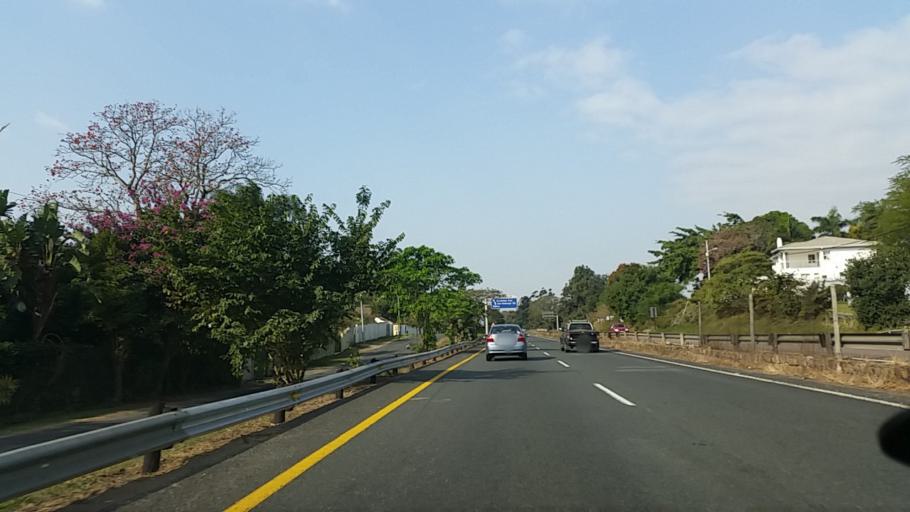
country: ZA
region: KwaZulu-Natal
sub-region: eThekwini Metropolitan Municipality
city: Berea
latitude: -29.8326
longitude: 30.9327
